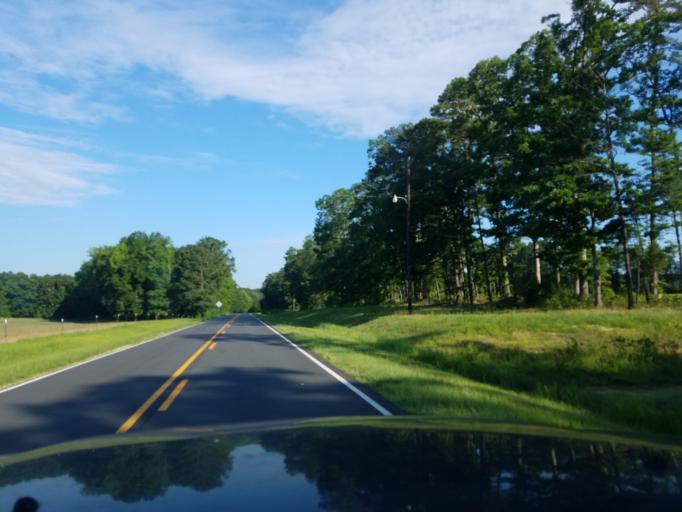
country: US
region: North Carolina
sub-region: Granville County
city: Butner
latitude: 36.1773
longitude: -78.7990
